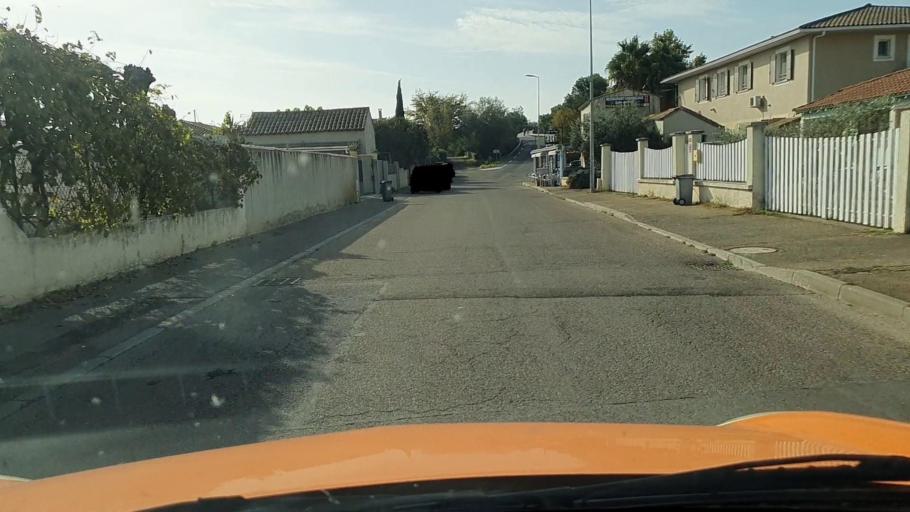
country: FR
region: Languedoc-Roussillon
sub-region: Departement du Gard
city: Vauvert
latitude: 43.6394
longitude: 4.2982
